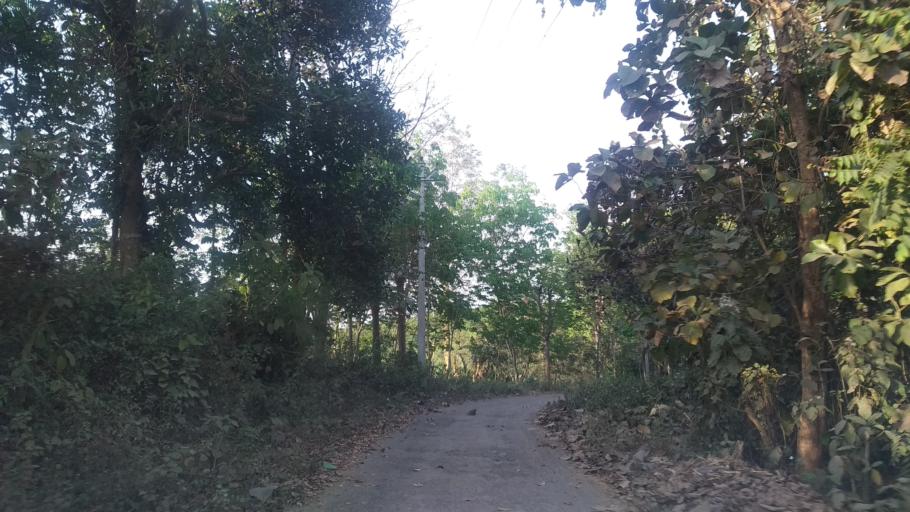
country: IN
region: Tripura
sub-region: West Tripura
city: Sonamura
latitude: 23.4441
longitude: 91.3720
